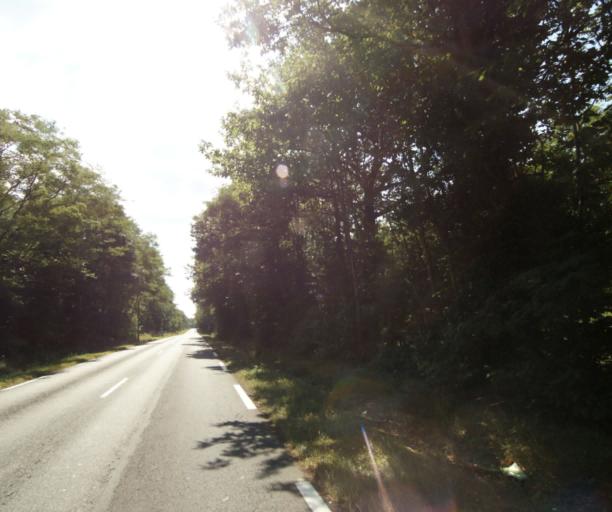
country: FR
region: Centre
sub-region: Departement du Loiret
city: Saint-Cyr-en-Val
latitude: 47.8212
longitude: 1.9851
